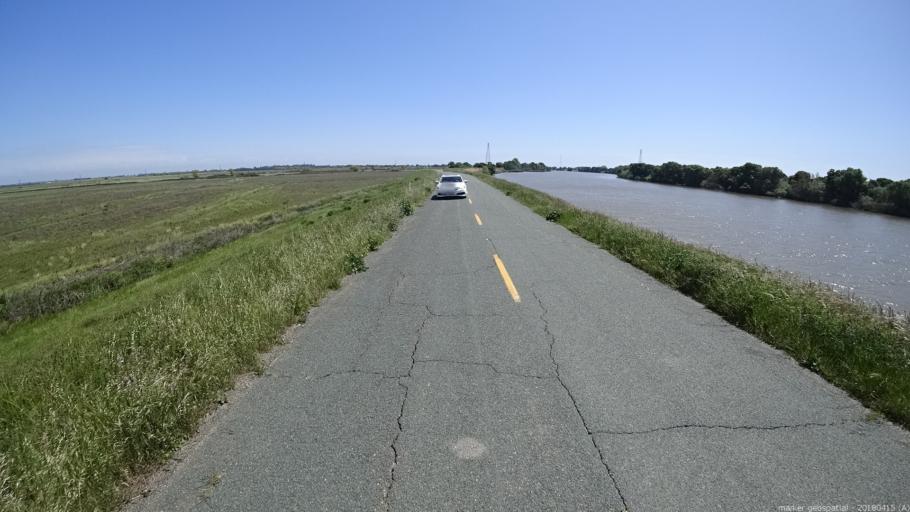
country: US
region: California
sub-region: Solano County
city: Rio Vista
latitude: 38.1729
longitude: -121.6362
